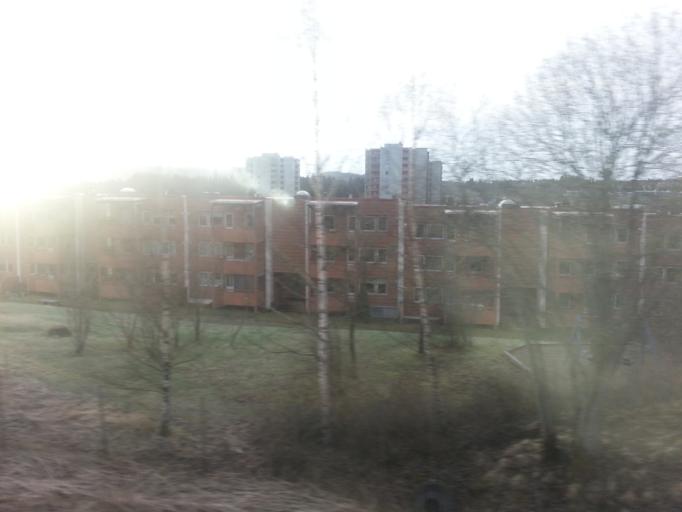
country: NO
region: Sor-Trondelag
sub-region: Trondheim
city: Trondheim
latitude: 63.3785
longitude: 10.3568
